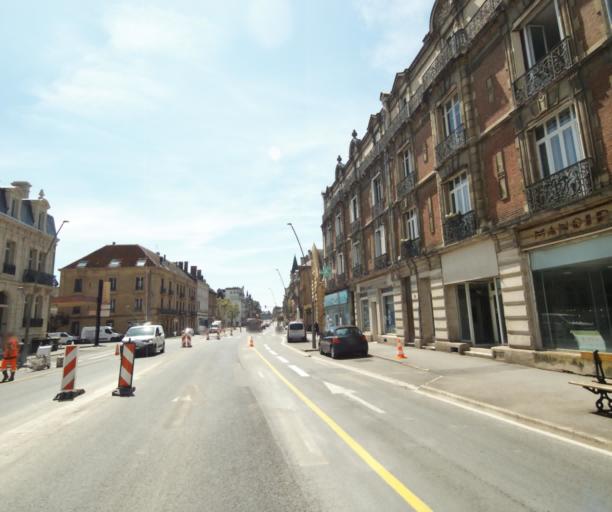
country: FR
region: Champagne-Ardenne
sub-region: Departement des Ardennes
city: Charleville-Mezieres
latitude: 49.7654
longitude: 4.7195
